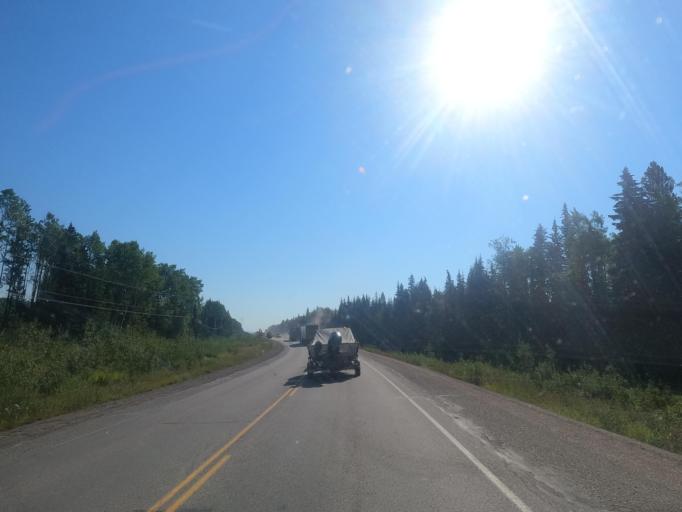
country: CA
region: British Columbia
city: Burns Lake
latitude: 54.1020
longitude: -125.3327
